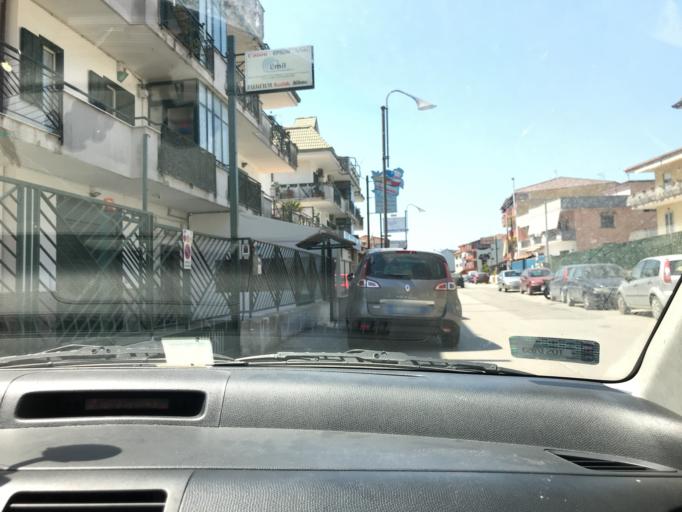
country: IT
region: Campania
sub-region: Provincia di Napoli
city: Villaricca
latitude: 40.9224
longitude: 14.1716
